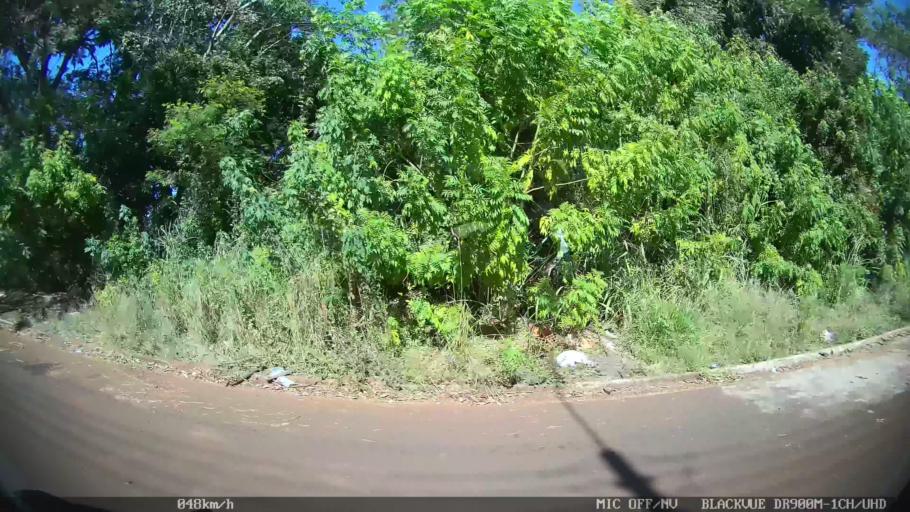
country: BR
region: Sao Paulo
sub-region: Batatais
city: Batatais
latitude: -20.8908
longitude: -47.5770
